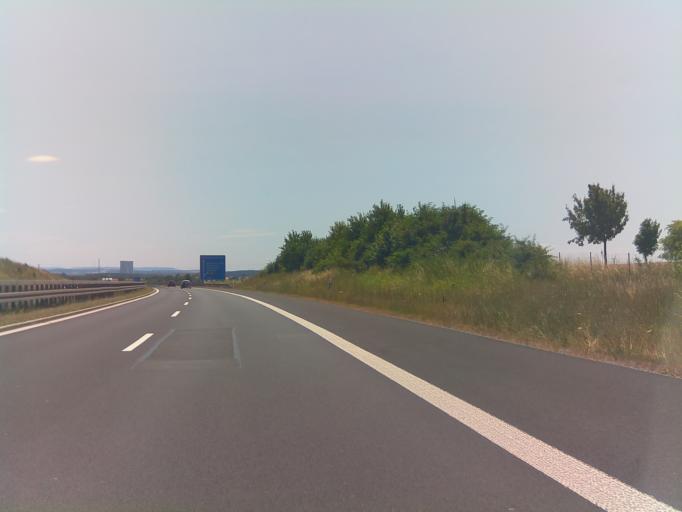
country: DE
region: Bavaria
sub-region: Regierungsbezirk Unterfranken
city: Euerbach
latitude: 50.0689
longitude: 10.1472
